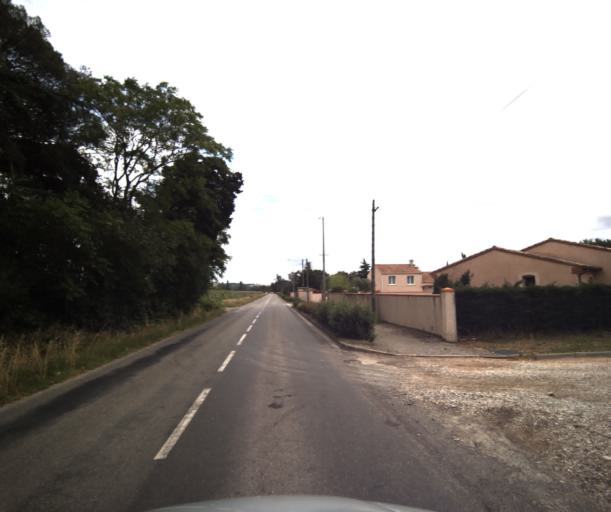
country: FR
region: Midi-Pyrenees
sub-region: Departement de la Haute-Garonne
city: Roquettes
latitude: 43.4901
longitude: 1.3846
